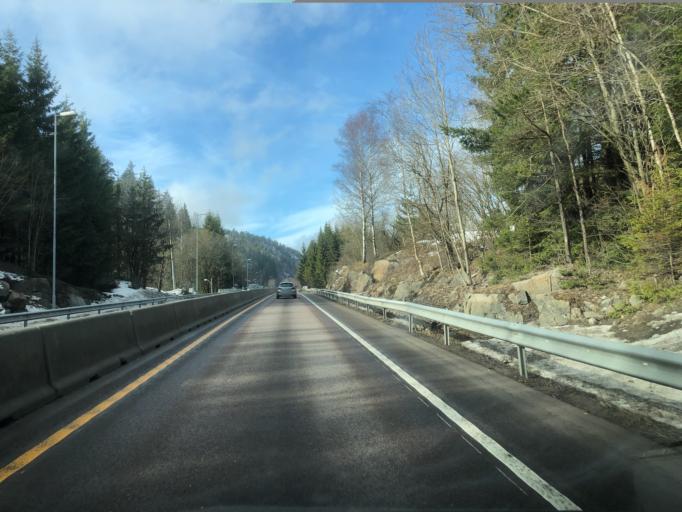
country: NO
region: Telemark
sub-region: Bamble
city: Langesund
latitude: 59.0950
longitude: 9.7843
